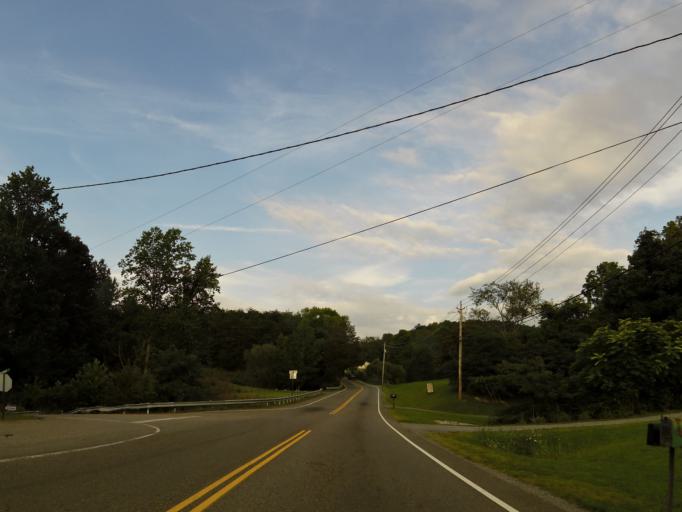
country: US
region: Tennessee
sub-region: Cocke County
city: Newport
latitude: 35.9570
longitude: -83.2848
